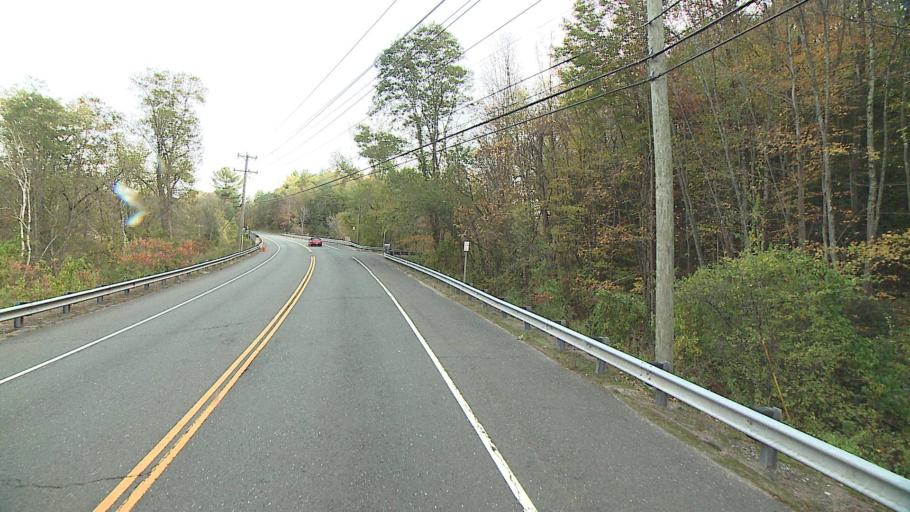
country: US
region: Connecticut
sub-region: Litchfield County
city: New Hartford Center
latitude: 41.8557
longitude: -72.9582
